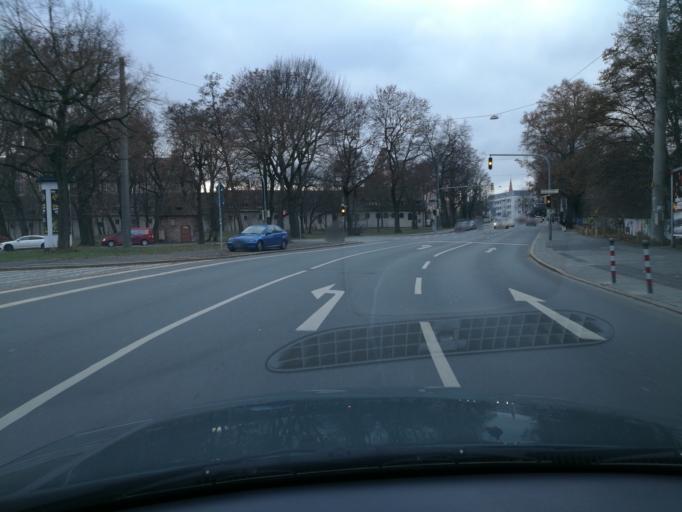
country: DE
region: Bavaria
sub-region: Regierungsbezirk Mittelfranken
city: Nuernberg
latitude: 49.4550
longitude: 11.0583
